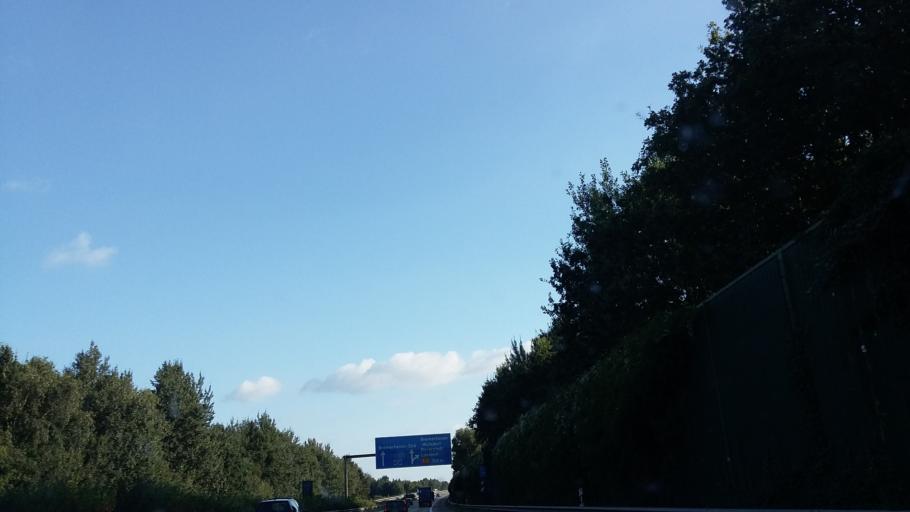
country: DE
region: Lower Saxony
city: Schiffdorf
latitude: 53.5058
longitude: 8.6289
